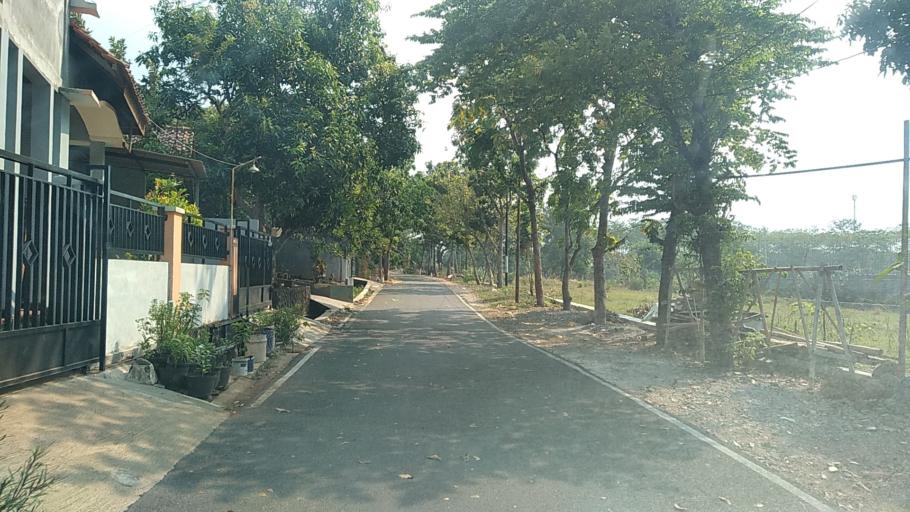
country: ID
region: Central Java
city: Semarang
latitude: -7.0669
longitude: 110.4360
